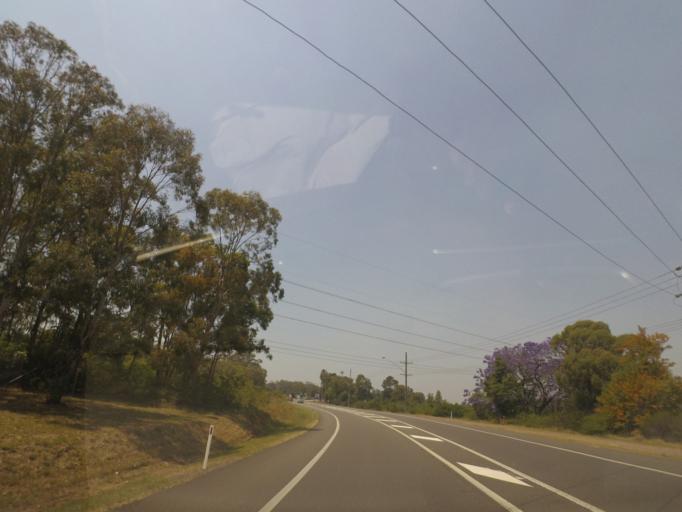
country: AU
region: New South Wales
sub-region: Newcastle
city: Beresfield
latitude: -32.8270
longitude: 151.7089
